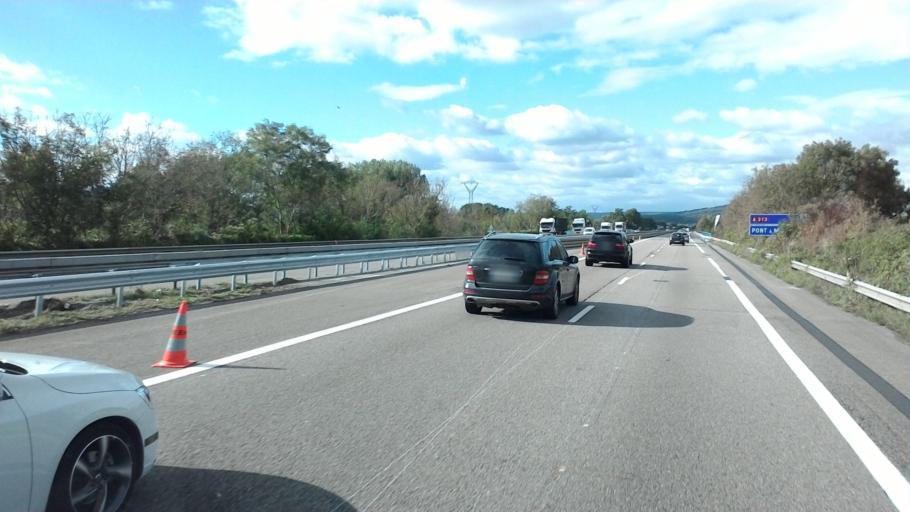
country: FR
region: Lorraine
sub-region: Departement de Meurthe-et-Moselle
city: Belleville
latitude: 48.8223
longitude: 6.1042
